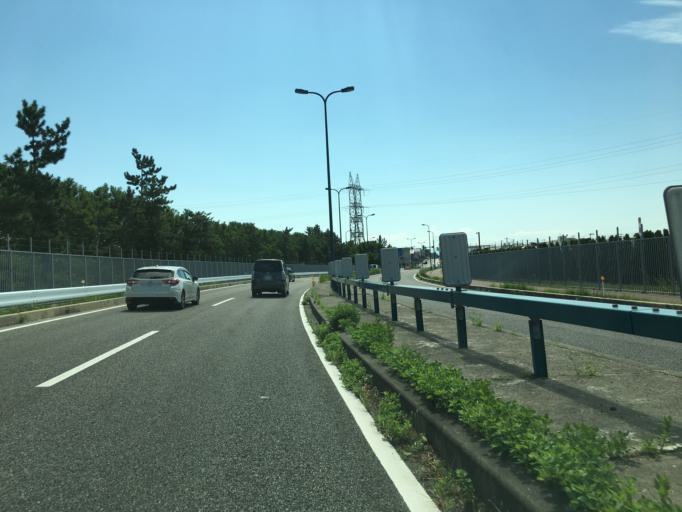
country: JP
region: Niigata
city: Niigata-shi
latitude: 37.9458
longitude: 139.0859
